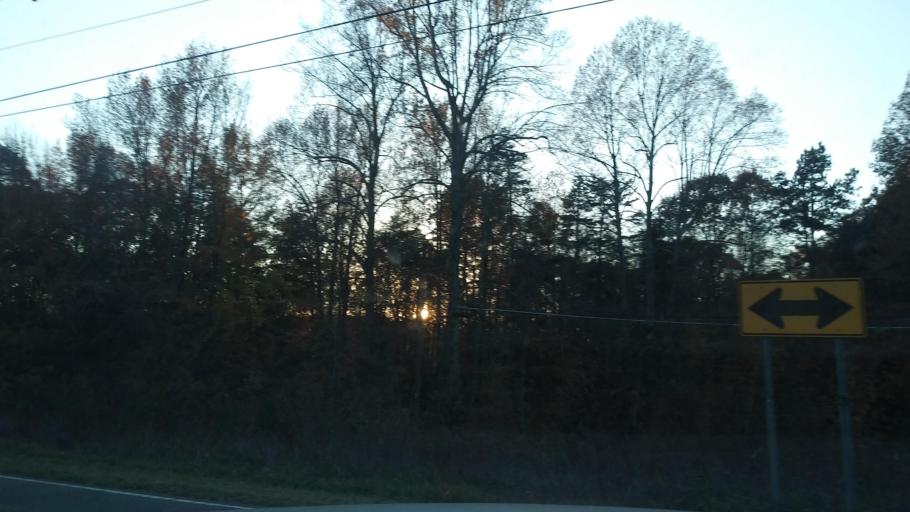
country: US
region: North Carolina
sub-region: Guilford County
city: Pleasant Garden
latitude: 36.0009
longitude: -79.7777
